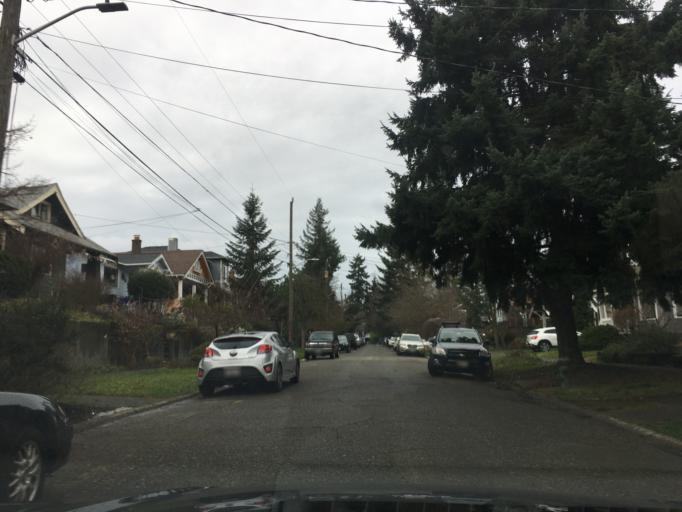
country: US
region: Washington
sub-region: King County
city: Seattle
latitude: 47.6637
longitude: -122.3291
